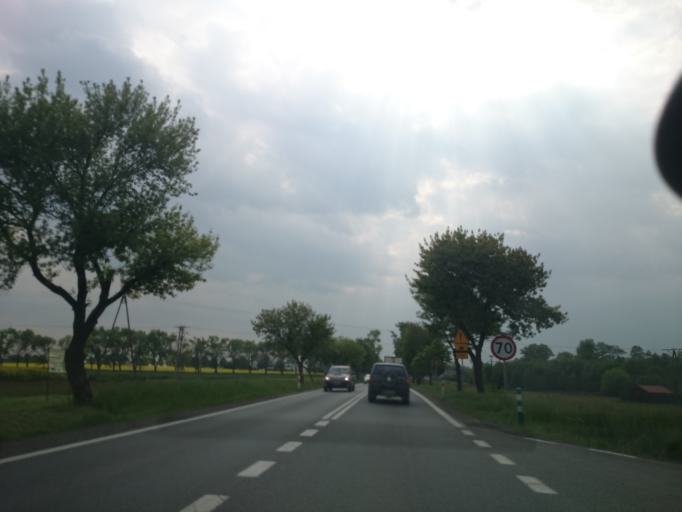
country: PL
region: Lower Silesian Voivodeship
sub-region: Powiat wroclawski
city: Kobierzyce
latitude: 50.9723
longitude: 16.9400
